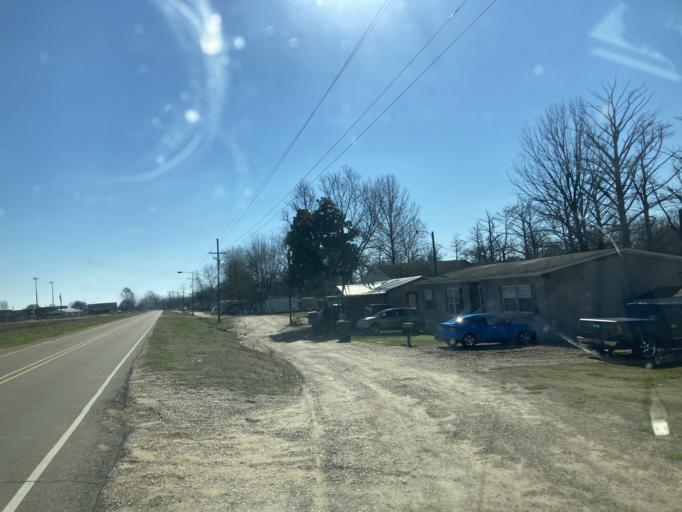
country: US
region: Mississippi
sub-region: Yazoo County
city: Yazoo City
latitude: 32.9763
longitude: -90.5900
